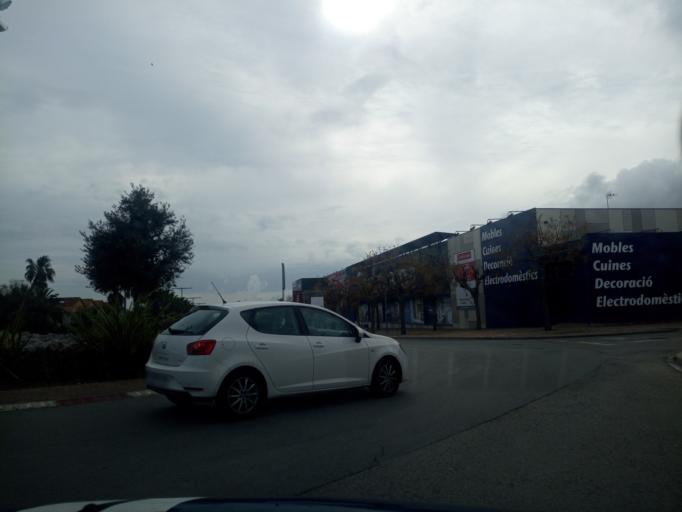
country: ES
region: Catalonia
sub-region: Provincia de Barcelona
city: Sant Pere de Ribes
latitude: 41.2290
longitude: 1.7672
